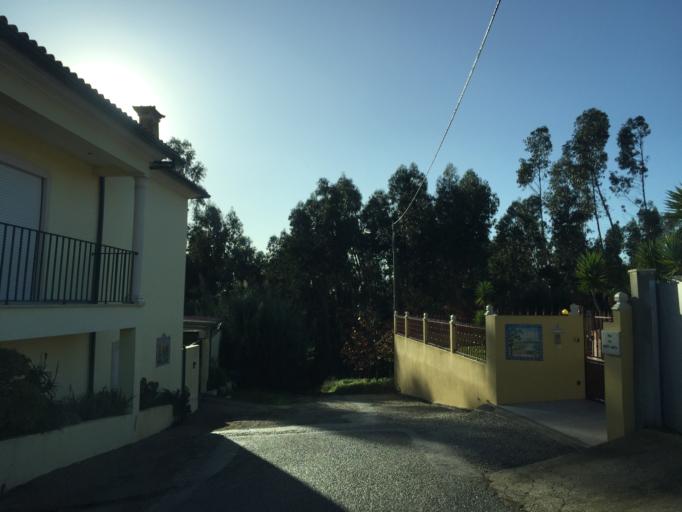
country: PT
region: Coimbra
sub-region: Figueira da Foz
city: Lavos
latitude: 40.0489
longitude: -8.7892
